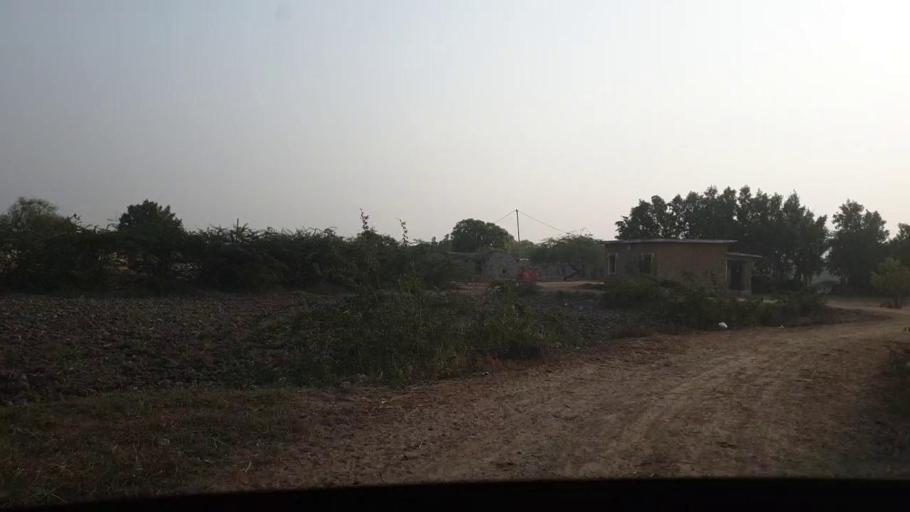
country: PK
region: Sindh
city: Jati
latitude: 24.2554
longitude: 68.1185
